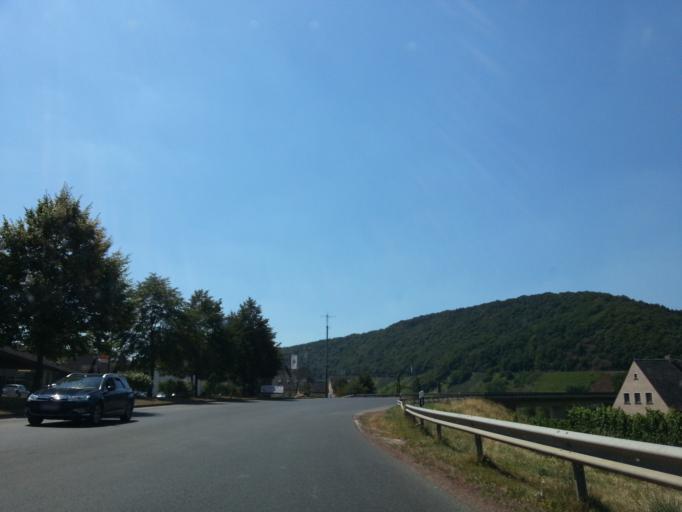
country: DE
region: Rheinland-Pfalz
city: Neumagen-Dhron
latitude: 49.8604
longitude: 6.8982
